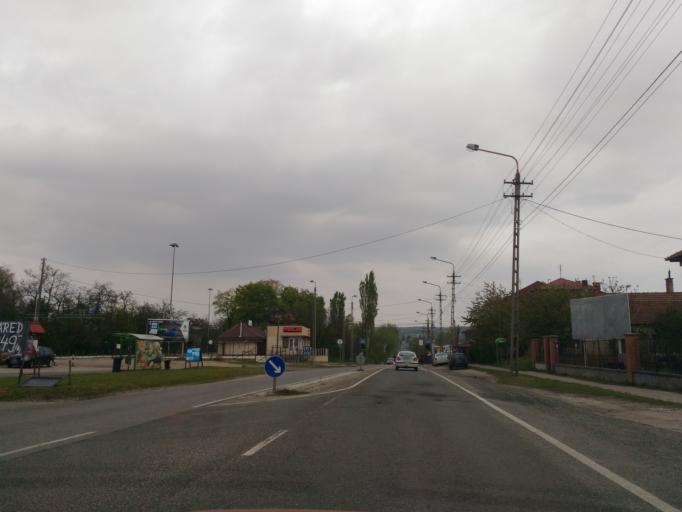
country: HU
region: Pest
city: Kistarcsa
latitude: 47.5521
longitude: 19.2703
